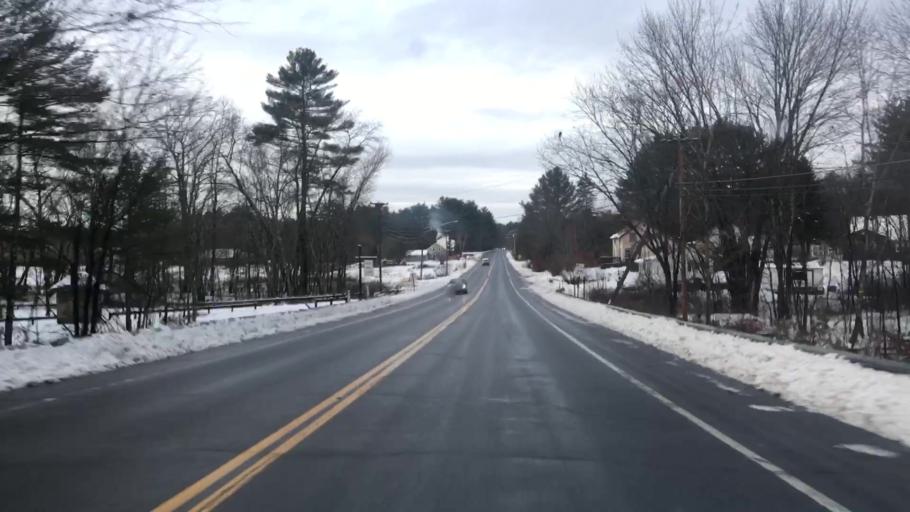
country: US
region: Maine
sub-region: York County
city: Limington
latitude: 43.7336
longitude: -70.6535
